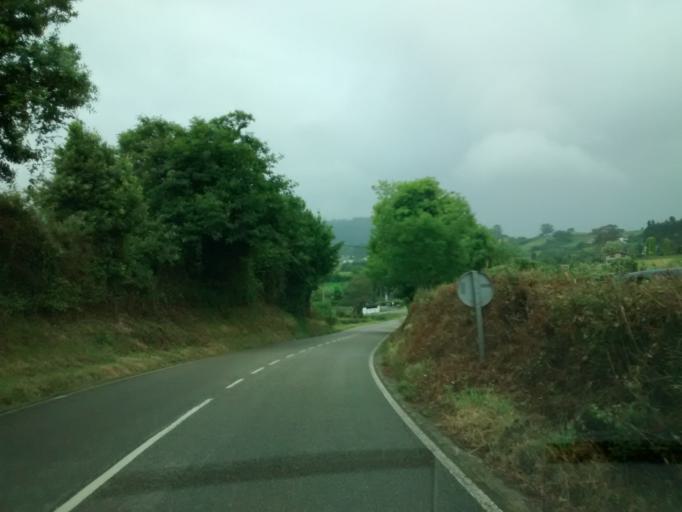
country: ES
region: Asturias
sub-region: Province of Asturias
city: Villaviciosa
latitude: 43.5232
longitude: -5.3721
